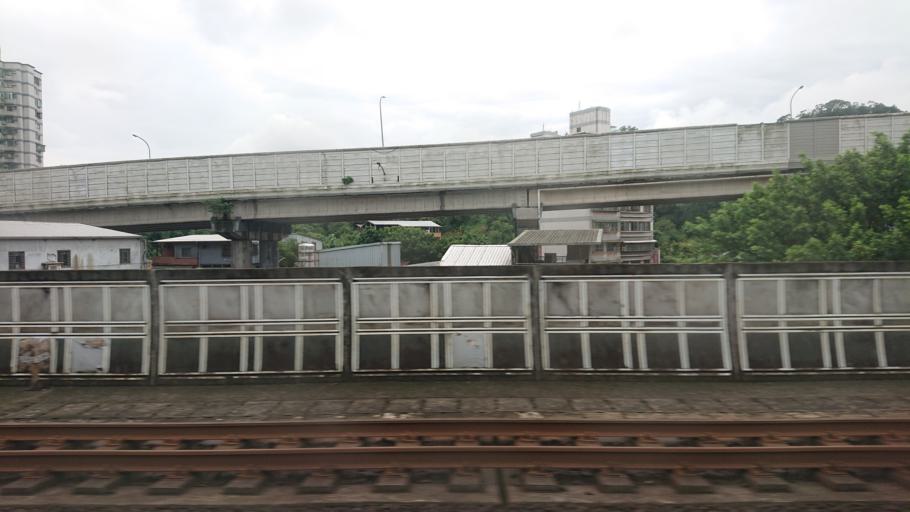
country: TW
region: Taiwan
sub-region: Keelung
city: Keelung
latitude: 25.0768
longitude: 121.6665
